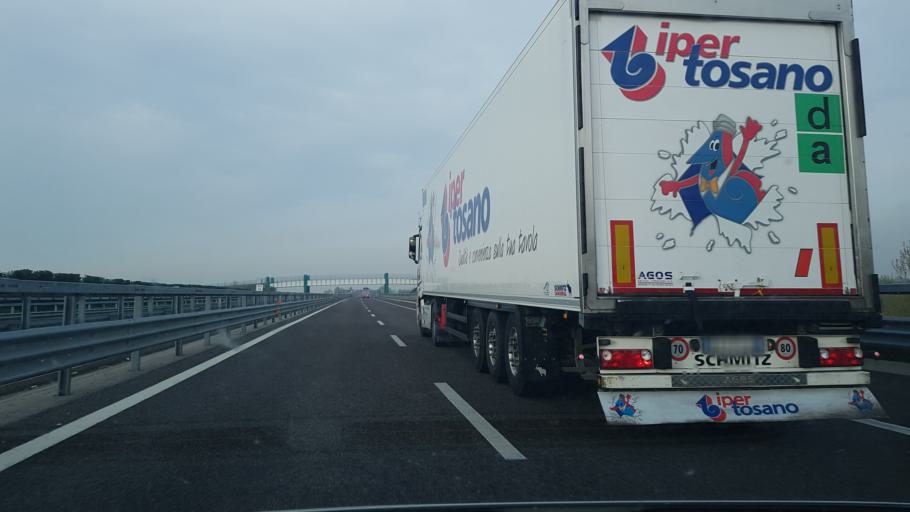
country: IT
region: Veneto
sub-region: Provincia di Vicenza
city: Albettone
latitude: 45.3555
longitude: 11.5992
